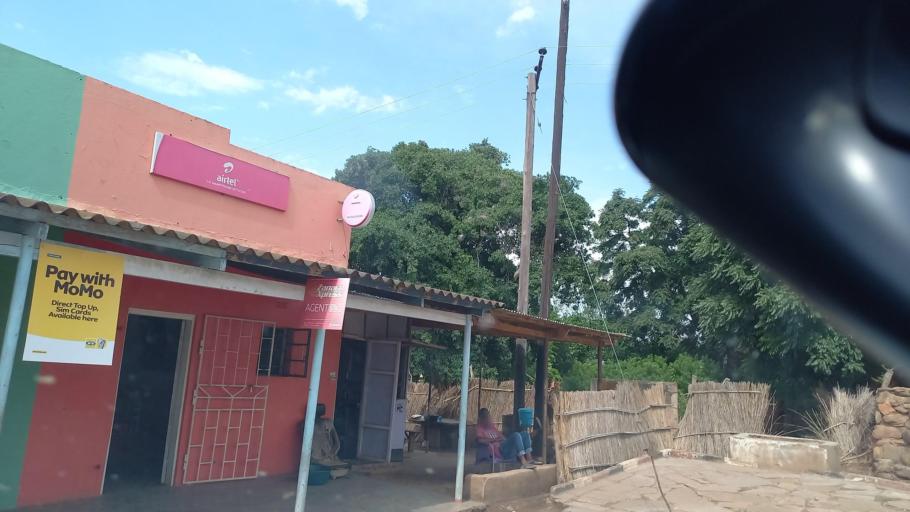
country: ZM
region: Lusaka
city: Kafue
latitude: -16.2282
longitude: 28.1421
